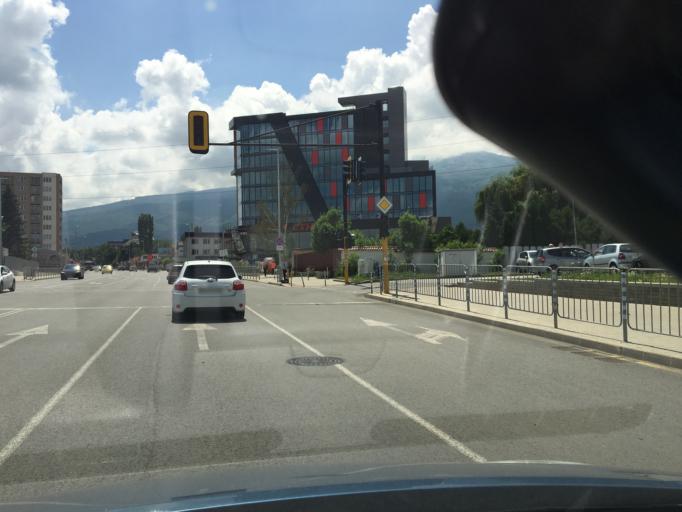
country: BG
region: Sofia-Capital
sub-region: Stolichna Obshtina
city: Sofia
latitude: 42.6561
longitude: 23.3158
